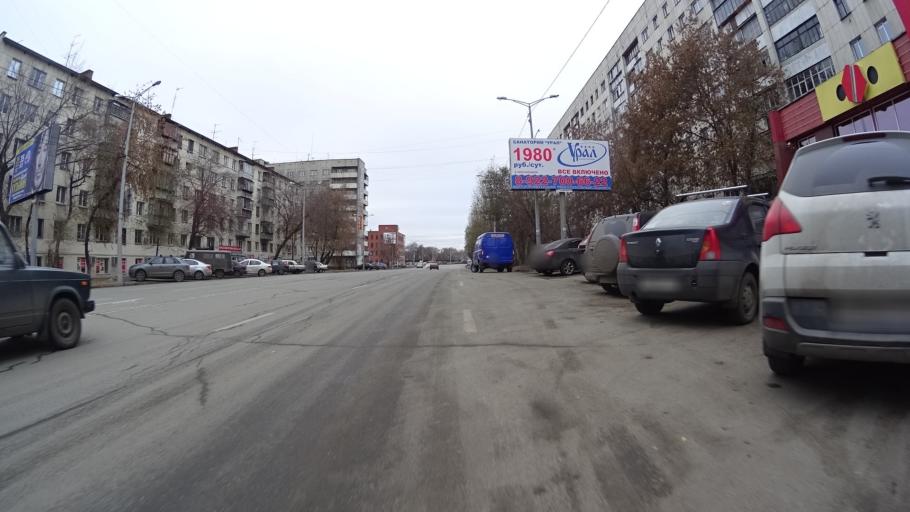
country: RU
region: Chelyabinsk
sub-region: Gorod Chelyabinsk
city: Chelyabinsk
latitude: 55.1558
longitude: 61.4179
